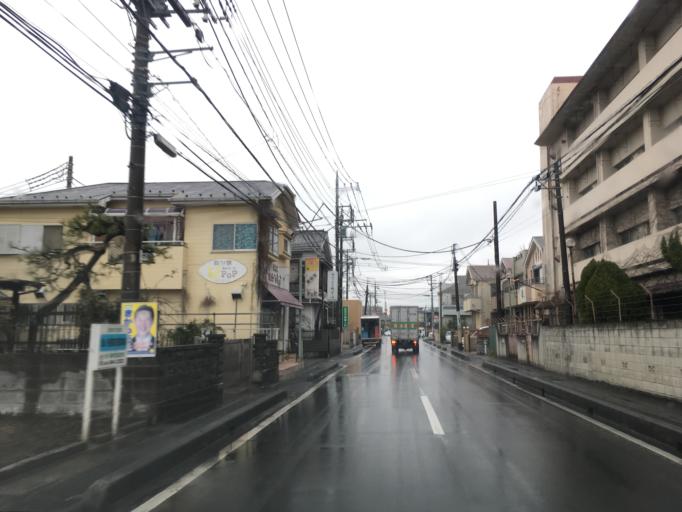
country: JP
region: Saitama
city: Koshigaya
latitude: 35.8899
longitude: 139.7799
